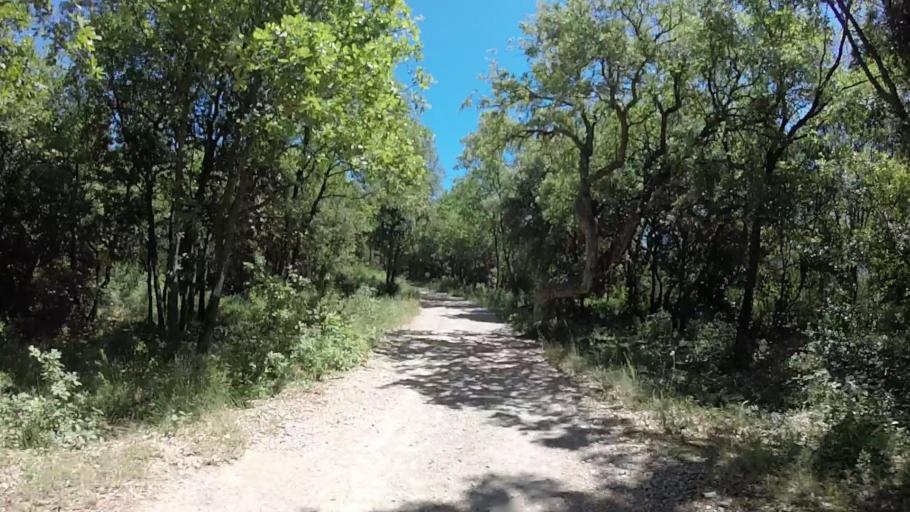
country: FR
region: Provence-Alpes-Cote d'Azur
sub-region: Departement des Alpes-Maritimes
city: Biot
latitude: 43.6299
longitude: 7.0511
